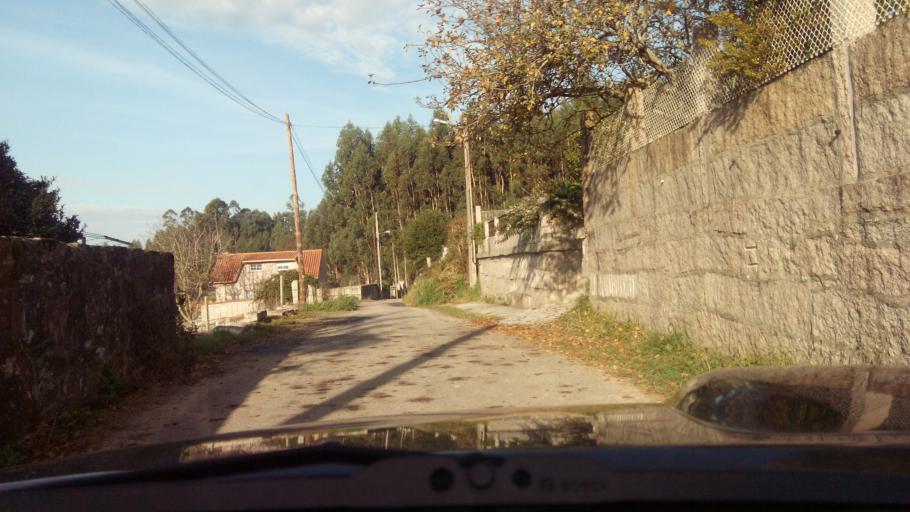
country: ES
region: Galicia
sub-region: Provincia de Pontevedra
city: Marin
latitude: 42.3629
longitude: -8.7103
